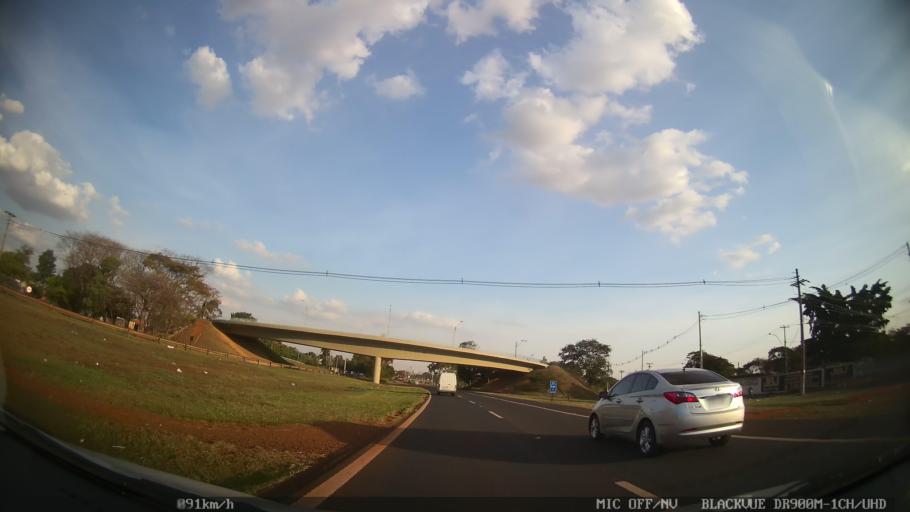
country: BR
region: Sao Paulo
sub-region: Ribeirao Preto
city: Ribeirao Preto
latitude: -21.1201
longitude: -47.7863
